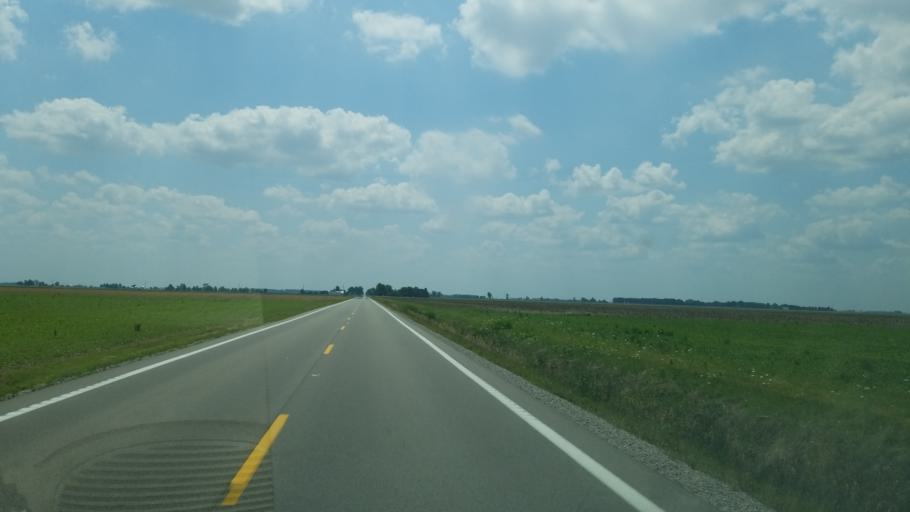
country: US
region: Ohio
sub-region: Henry County
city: Deshler
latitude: 41.3192
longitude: -83.9413
